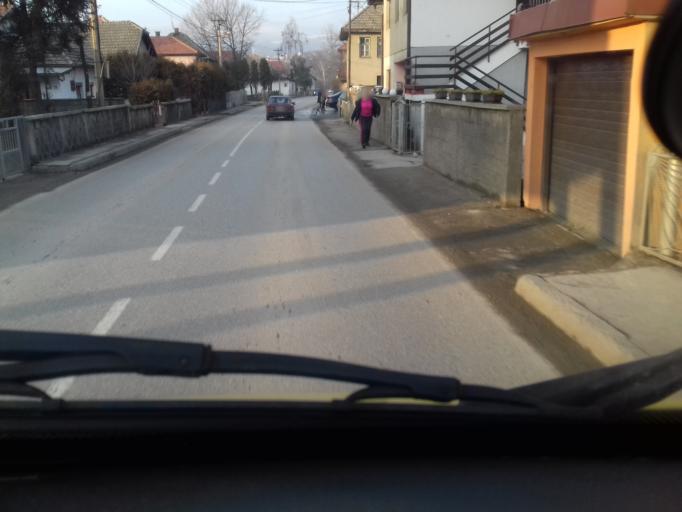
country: BA
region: Federation of Bosnia and Herzegovina
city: Kakanj
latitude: 44.1159
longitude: 18.1168
